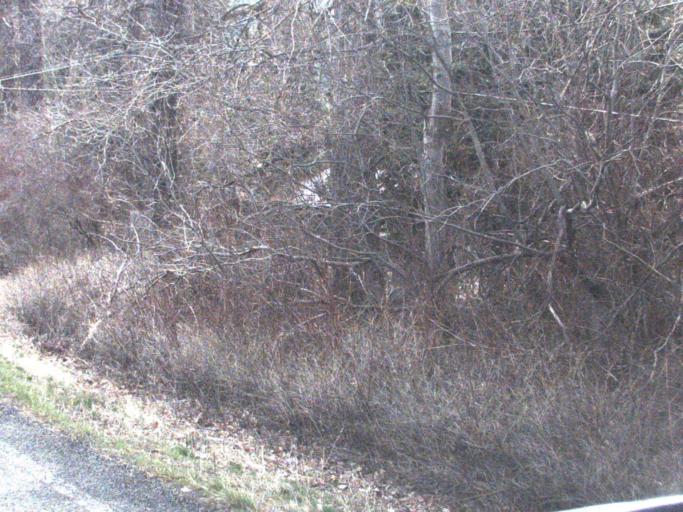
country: US
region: Washington
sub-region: Yakima County
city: Tieton
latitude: 46.8799
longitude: -120.9808
